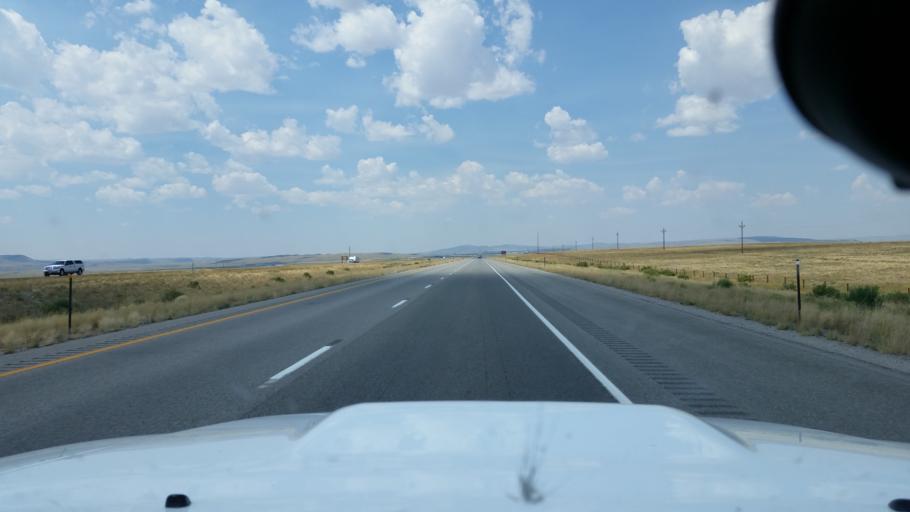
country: US
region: Wyoming
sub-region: Carbon County
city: Rawlins
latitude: 41.7600
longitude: -106.9929
